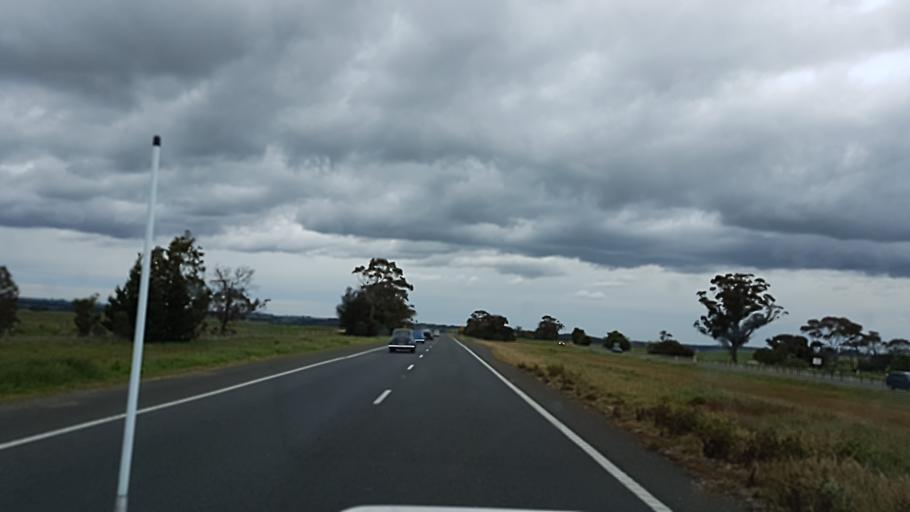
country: AU
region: Victoria
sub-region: Moorabool
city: Bacchus Marsh
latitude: -37.6011
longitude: 144.2739
